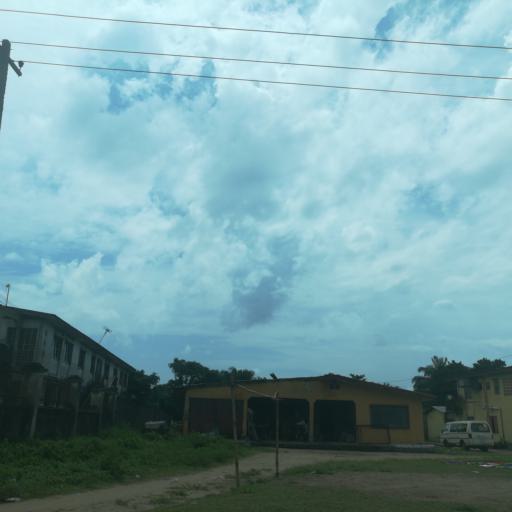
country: NG
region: Lagos
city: Ejirin
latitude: 6.6249
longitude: 3.7058
